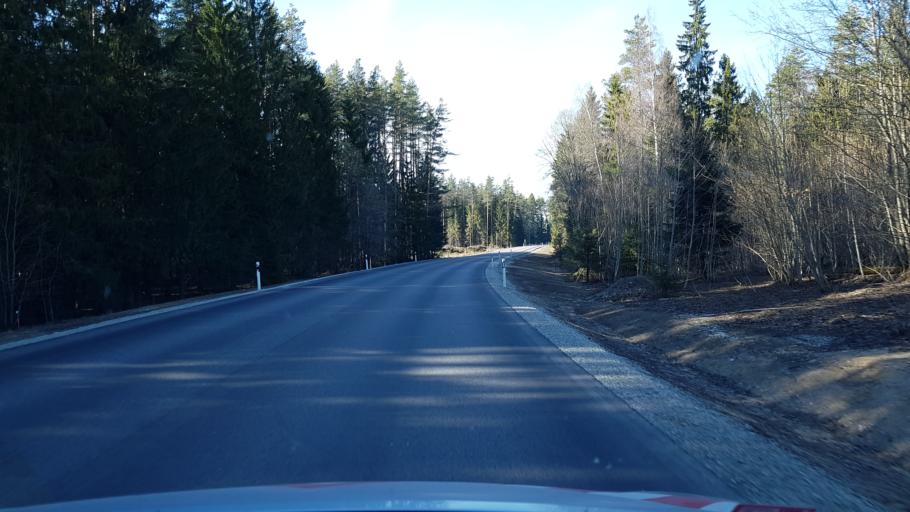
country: EE
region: Laeaene-Virumaa
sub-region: Vinni vald
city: Vinni
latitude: 59.1346
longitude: 26.5996
